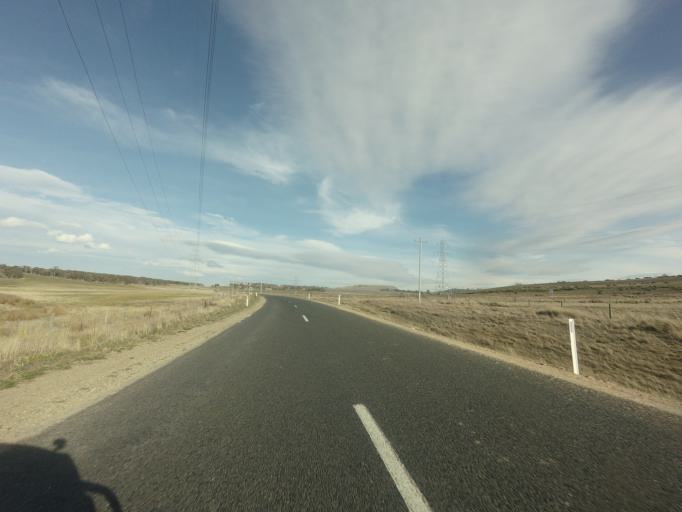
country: AU
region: Tasmania
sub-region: Derwent Valley
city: New Norfolk
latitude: -42.2617
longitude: 146.9376
